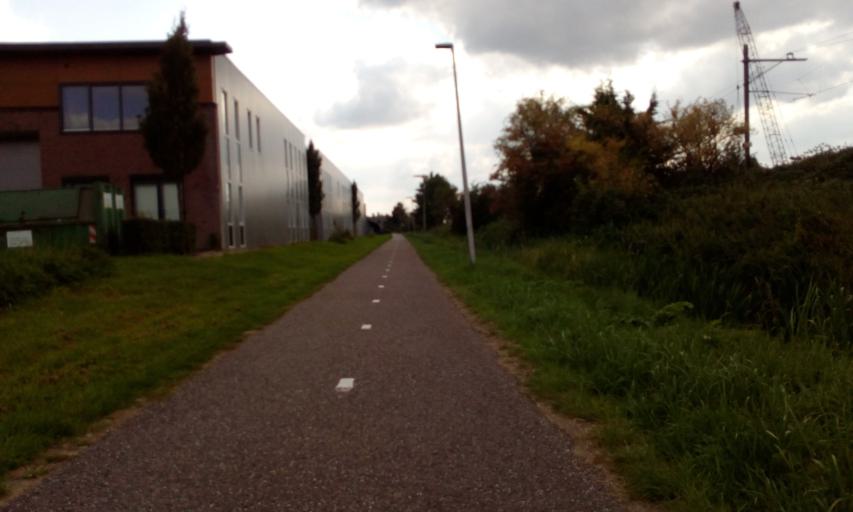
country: NL
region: South Holland
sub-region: Gemeente Waddinxveen
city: Waddinxveen
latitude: 52.0350
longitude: 4.6498
